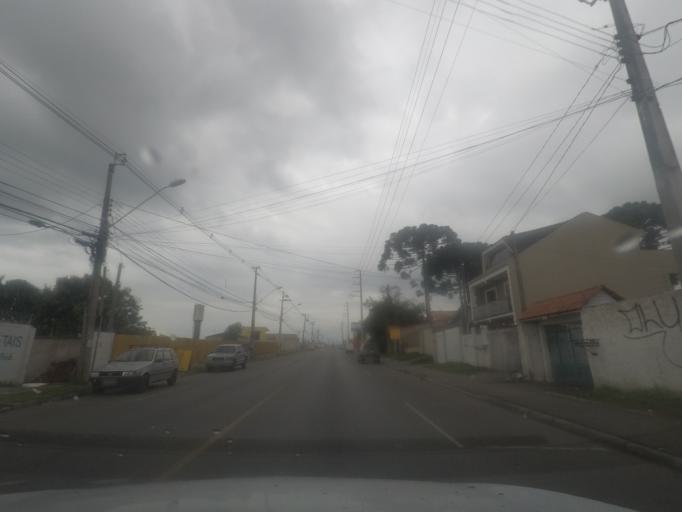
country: BR
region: Parana
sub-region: Sao Jose Dos Pinhais
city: Sao Jose dos Pinhais
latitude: -25.5554
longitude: -49.2530
